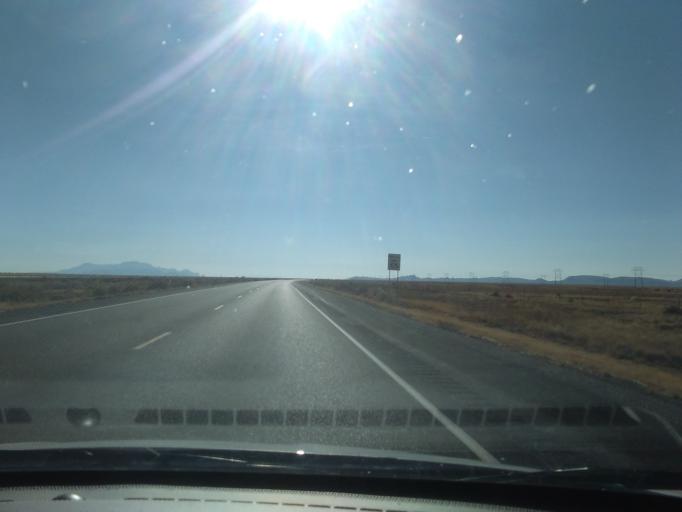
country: US
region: New Mexico
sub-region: Dona Ana County
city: Hatch
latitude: 32.5322
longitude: -107.4885
